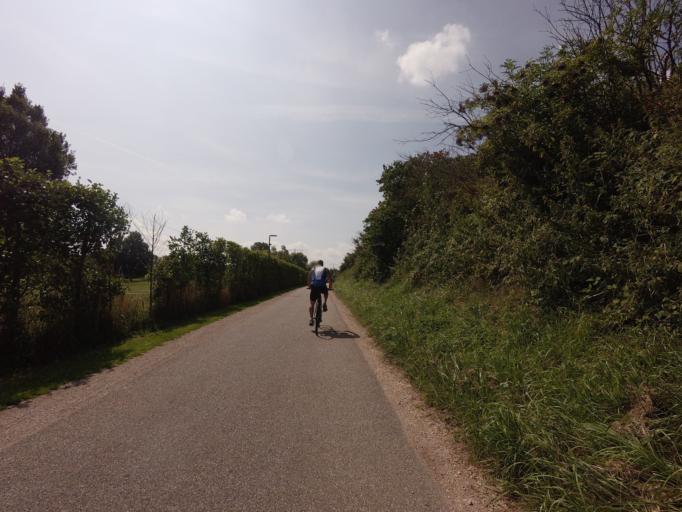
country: NL
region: South Holland
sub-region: Gemeente Sliedrecht
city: Sliedrecht
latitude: 51.8139
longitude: 4.7422
